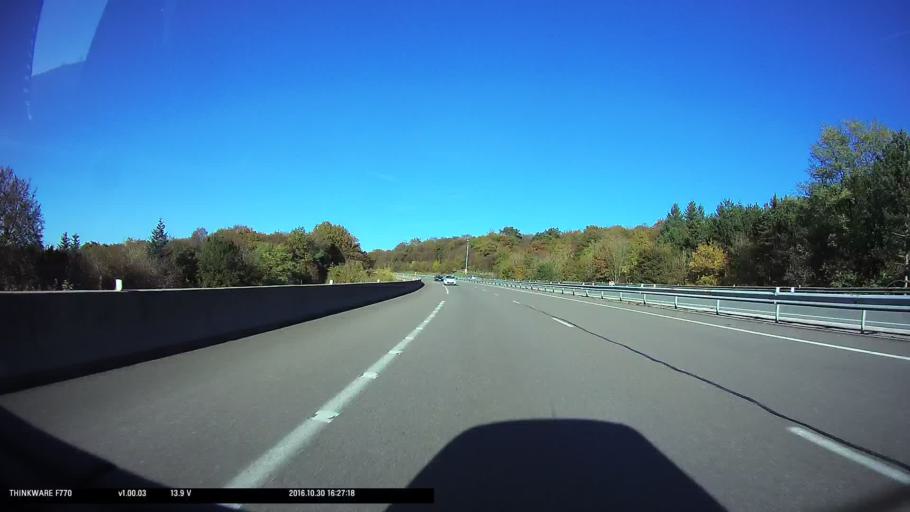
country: FR
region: Franche-Comte
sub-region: Departement du Doubs
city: Baume-les-Dames
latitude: 47.3515
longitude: 6.3147
